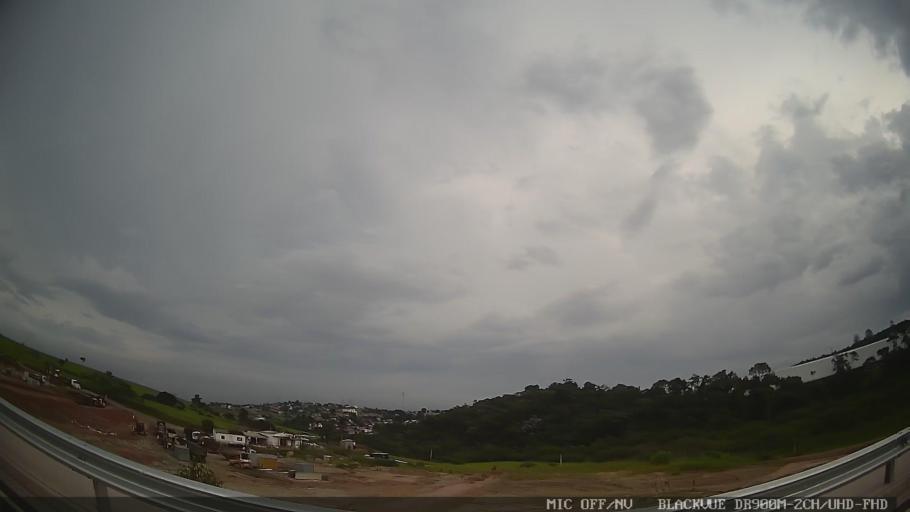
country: BR
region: Sao Paulo
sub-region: Aruja
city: Aruja
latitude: -23.4341
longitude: -46.2690
